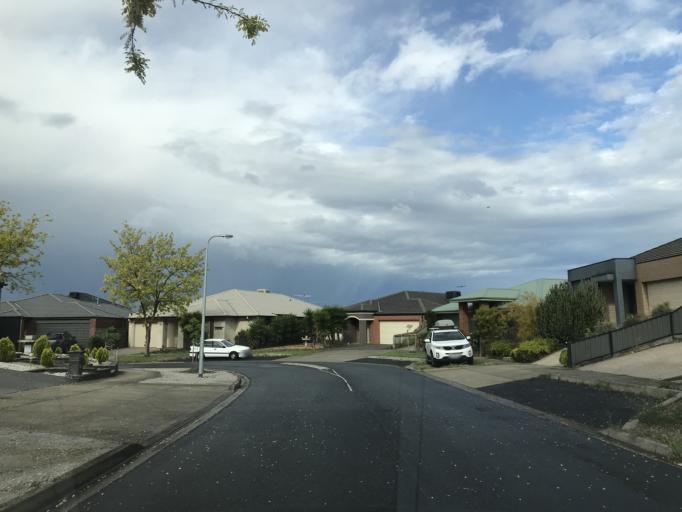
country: AU
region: Victoria
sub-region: Brimbank
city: Derrimut
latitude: -37.7883
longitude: 144.7692
